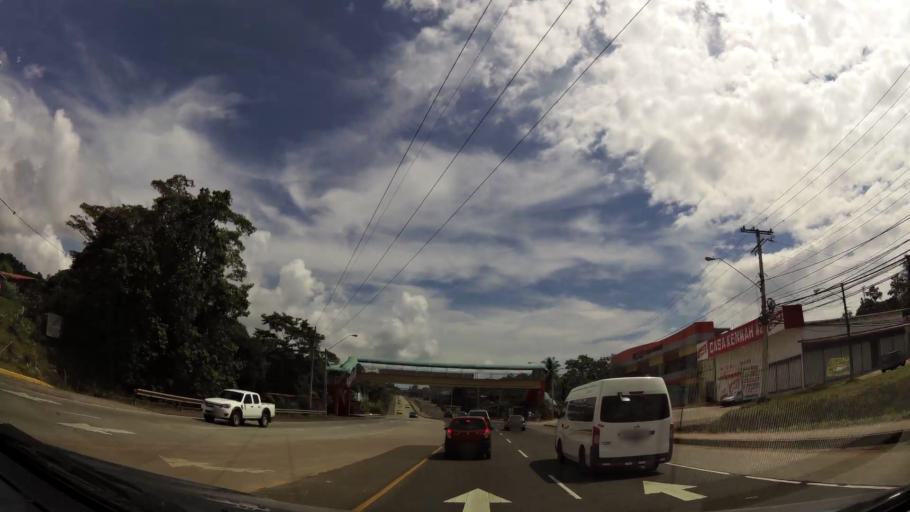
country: PA
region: Panama
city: Vista Alegre
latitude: 8.9331
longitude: -79.6945
